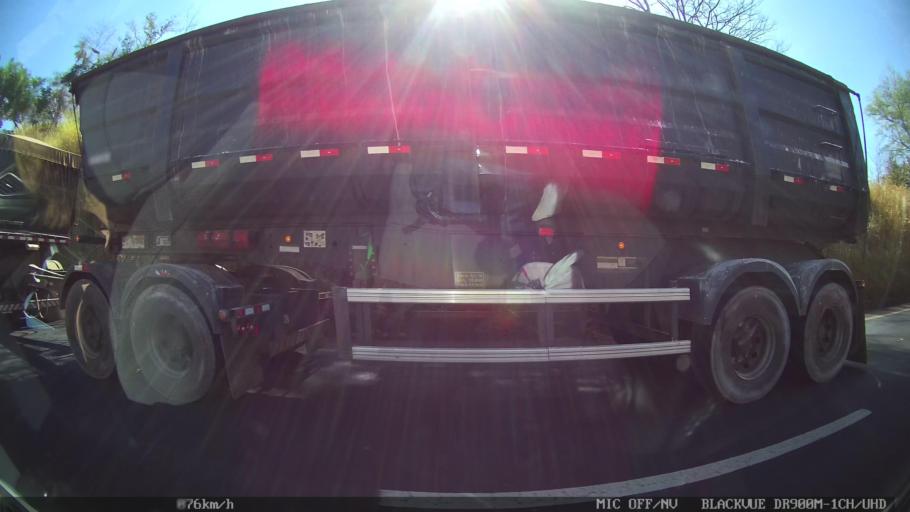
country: BR
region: Sao Paulo
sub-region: Barretos
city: Barretos
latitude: -20.5959
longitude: -48.7177
